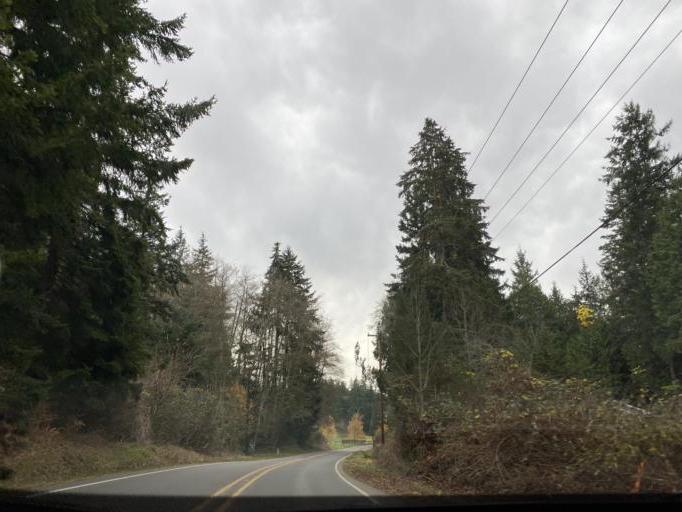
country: US
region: Washington
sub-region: Island County
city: Freeland
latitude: 48.0133
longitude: -122.5145
